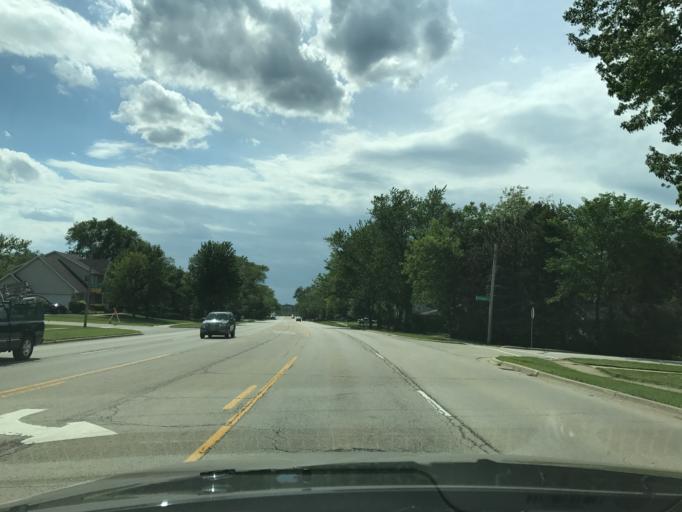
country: US
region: Illinois
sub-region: DuPage County
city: Lisle
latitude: 41.7870
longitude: -88.0651
